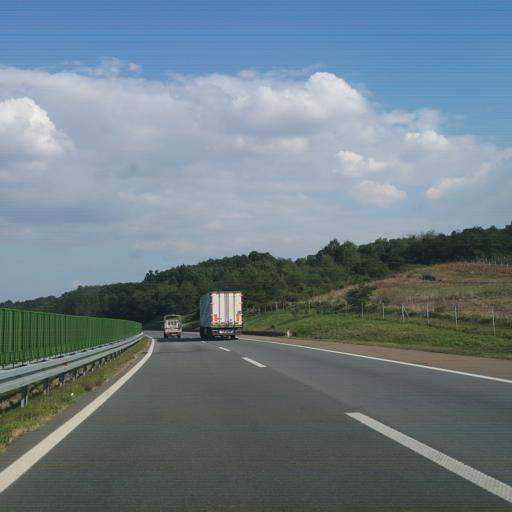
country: RS
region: Central Serbia
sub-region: Podunavski Okrug
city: Smederevo
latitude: 44.5726
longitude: 20.9163
